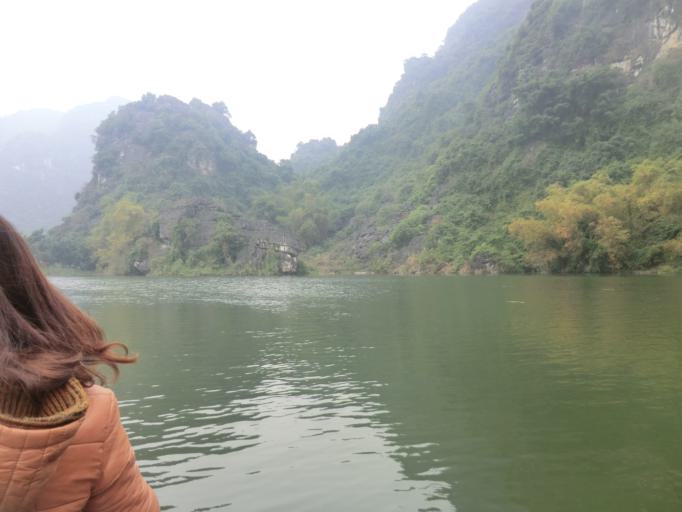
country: VN
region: Ninh Binh
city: Thi Tran Thien Ton
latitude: 20.2613
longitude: 105.9087
